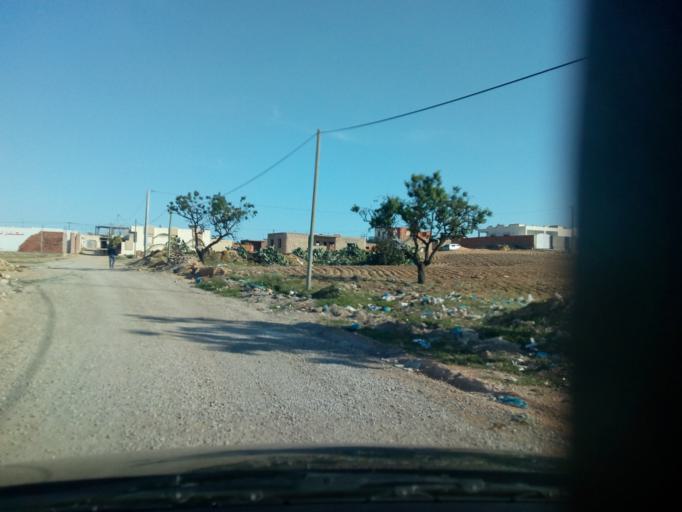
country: TN
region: Safaqis
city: Sfax
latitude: 34.7288
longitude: 10.6245
